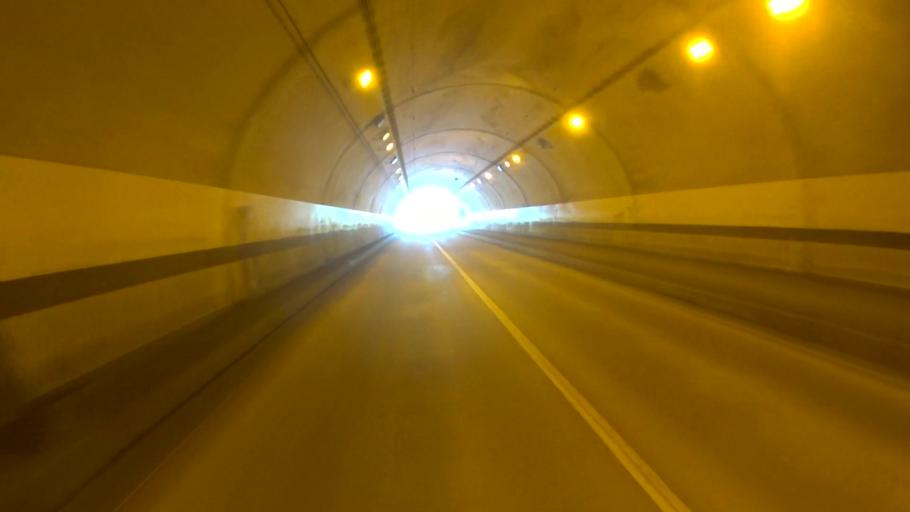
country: JP
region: Kyoto
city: Miyazu
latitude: 35.6629
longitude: 135.2600
